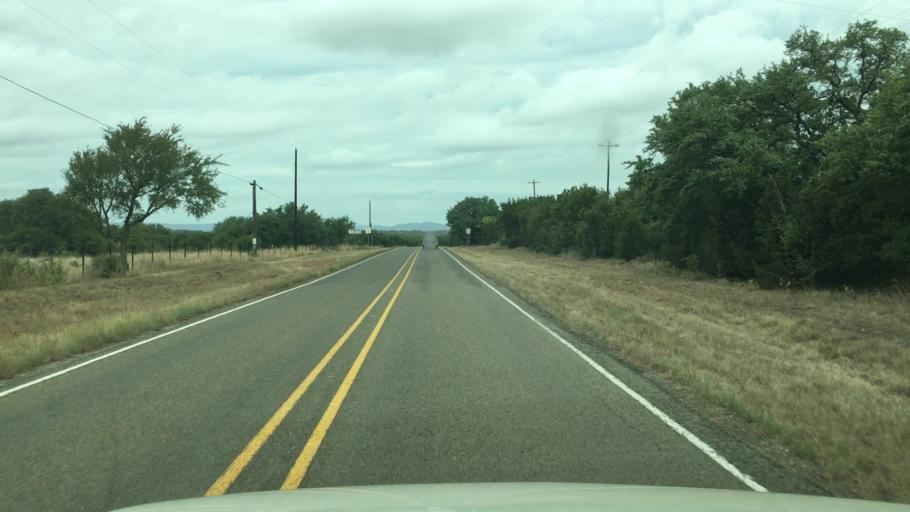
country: US
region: Texas
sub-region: Llano County
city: Horseshoe Bay
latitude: 30.4683
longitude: -98.4128
